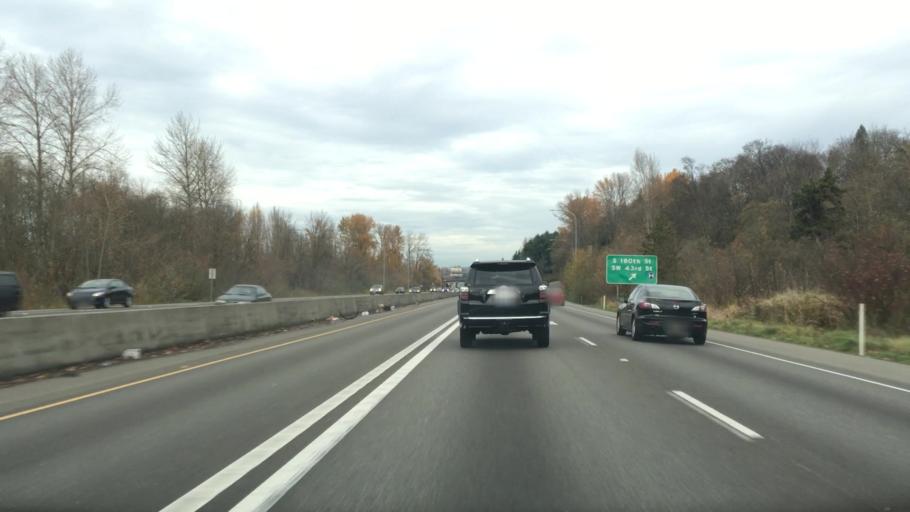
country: US
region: Washington
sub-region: King County
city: Renton
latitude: 47.4354
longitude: -122.2189
